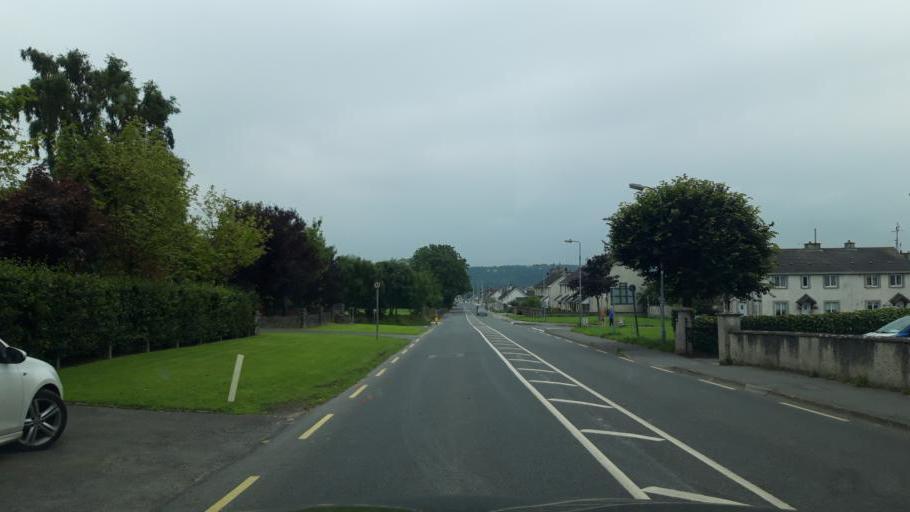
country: IE
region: Munster
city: Fethard
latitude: 52.4715
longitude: -7.6916
